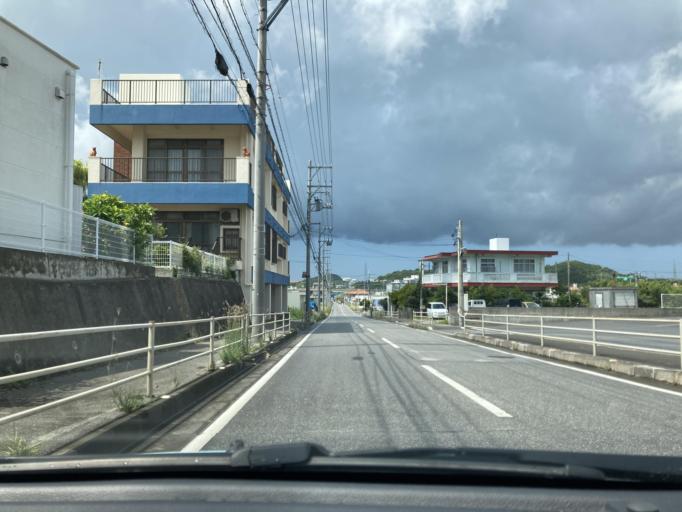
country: JP
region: Okinawa
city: Tomigusuku
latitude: 26.1810
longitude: 127.7419
